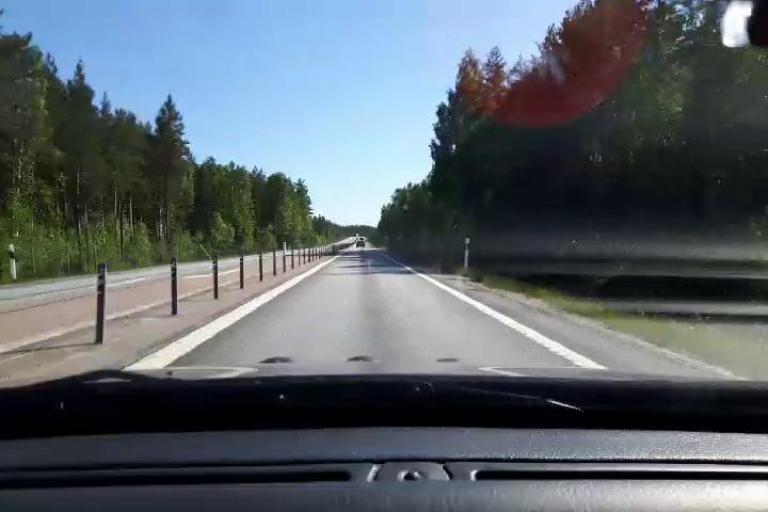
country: SE
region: Gaevleborg
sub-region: Soderhamns Kommun
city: Ljusne
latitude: 61.1226
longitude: 17.0144
